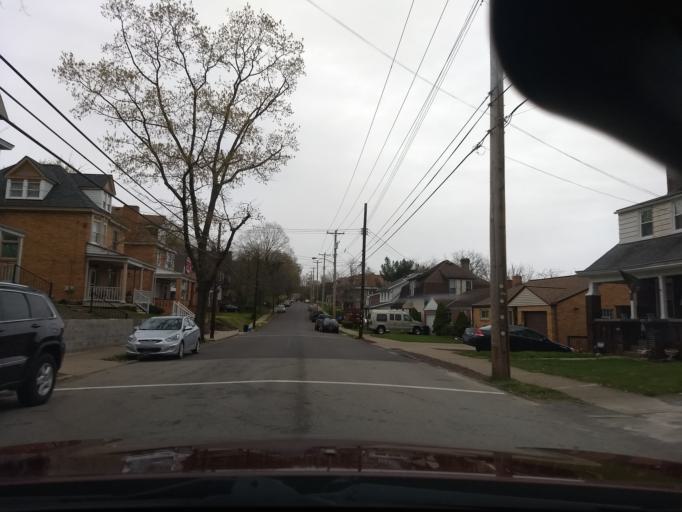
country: US
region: Pennsylvania
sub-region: Allegheny County
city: Ingram
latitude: 40.4473
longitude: -80.0765
